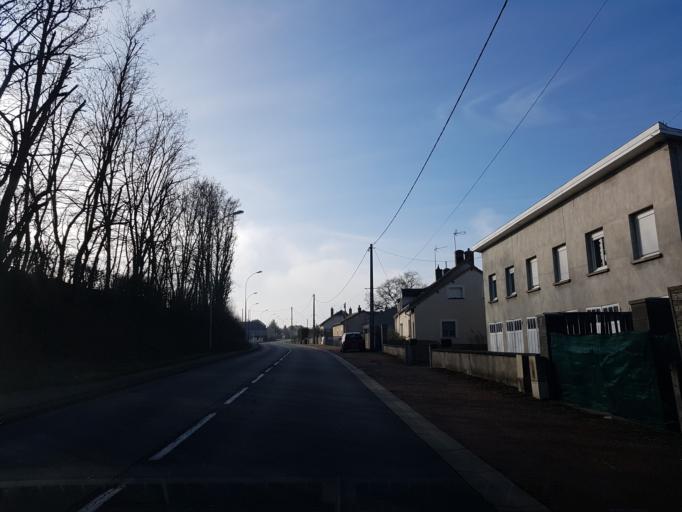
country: FR
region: Bourgogne
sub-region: Departement de Saone-et-Loire
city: Gueugnon
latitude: 46.5976
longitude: 4.0468
